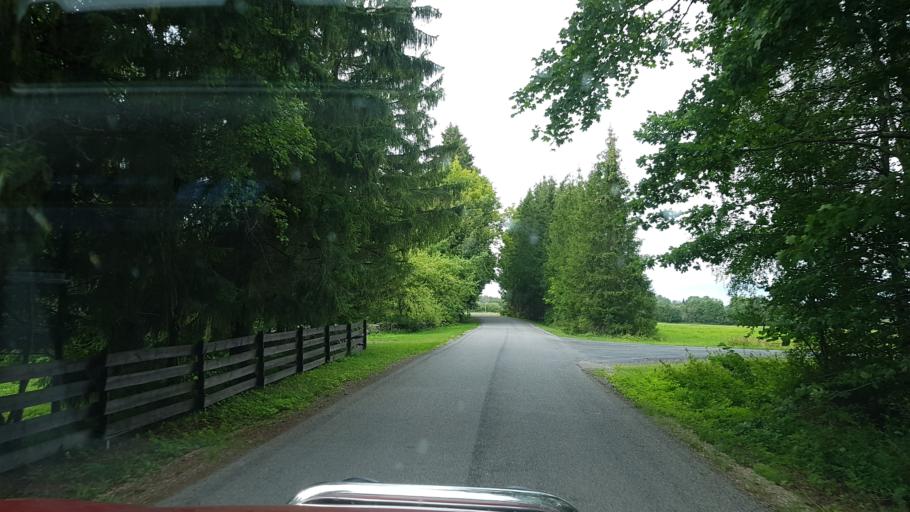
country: EE
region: Laeaene
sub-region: Ridala Parish
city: Uuemoisa
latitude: 58.9766
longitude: 23.7697
